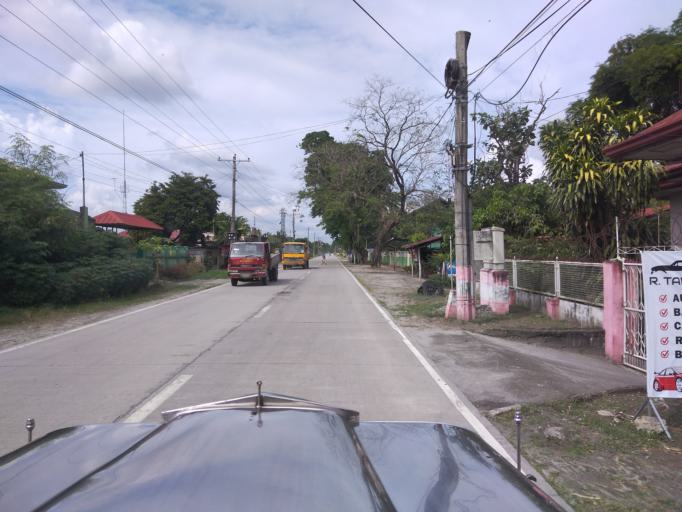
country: PH
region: Central Luzon
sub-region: Province of Pampanga
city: San Patricio
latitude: 15.0919
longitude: 120.7126
